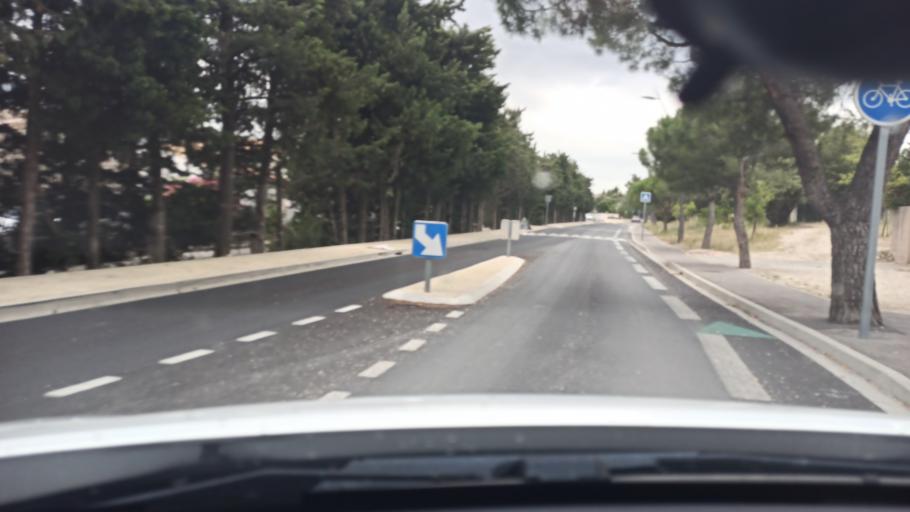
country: FR
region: Languedoc-Roussillon
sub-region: Departement du Gard
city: Les Angles
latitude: 43.9642
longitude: 4.7608
